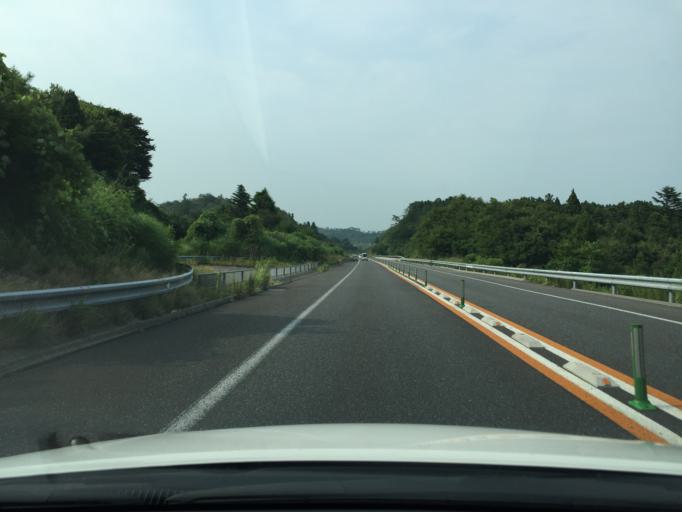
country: JP
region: Fukushima
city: Iwaki
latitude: 37.1580
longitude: 140.9665
